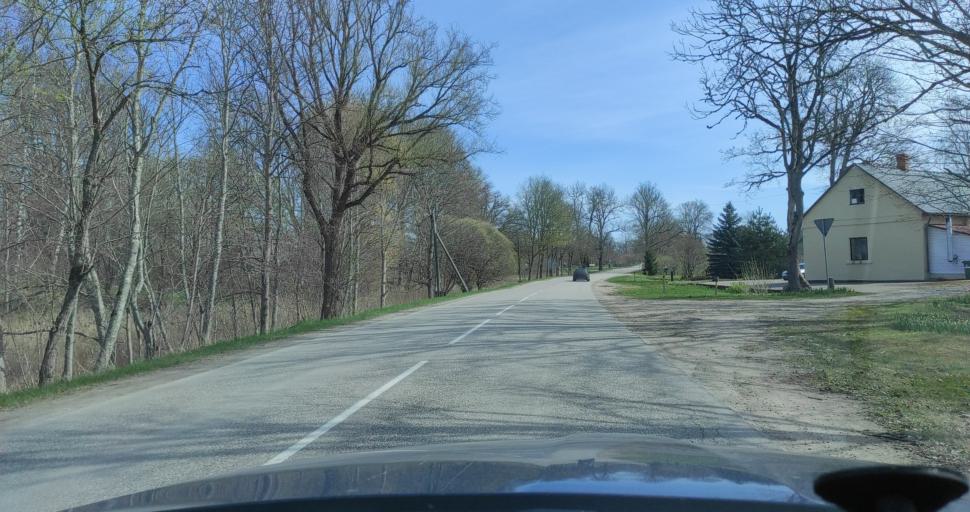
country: LV
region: Talsu Rajons
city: Talsi
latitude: 57.2253
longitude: 22.5170
